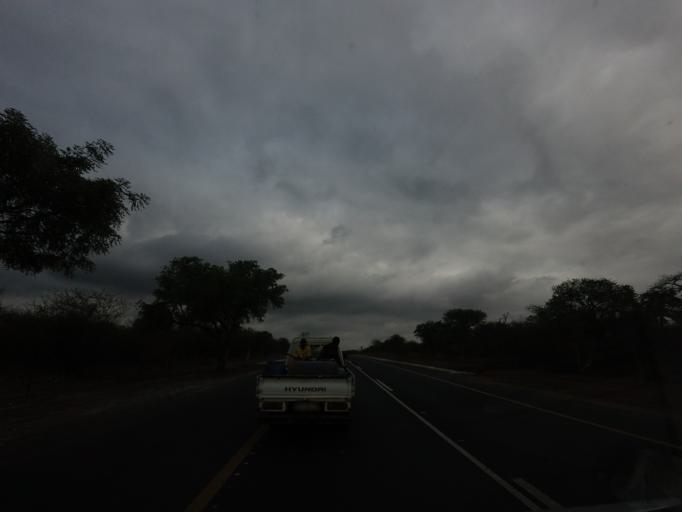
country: ZA
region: Mpumalanga
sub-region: Ehlanzeni District
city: Komatipoort
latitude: -25.4407
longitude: 31.7380
